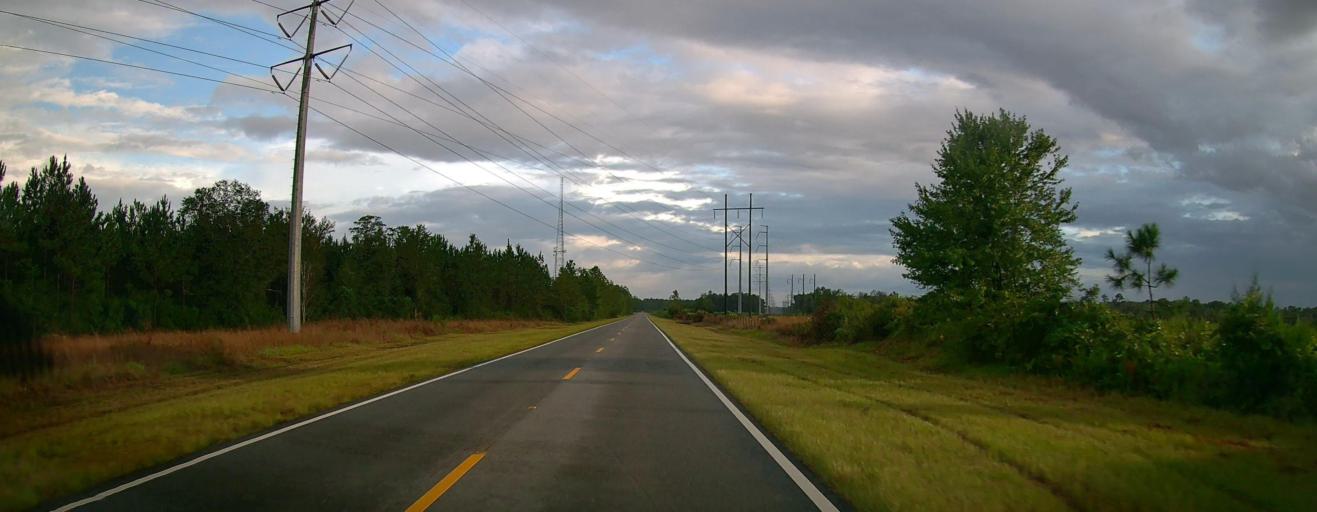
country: US
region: Georgia
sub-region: Ware County
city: Deenwood
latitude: 31.2038
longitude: -82.4014
